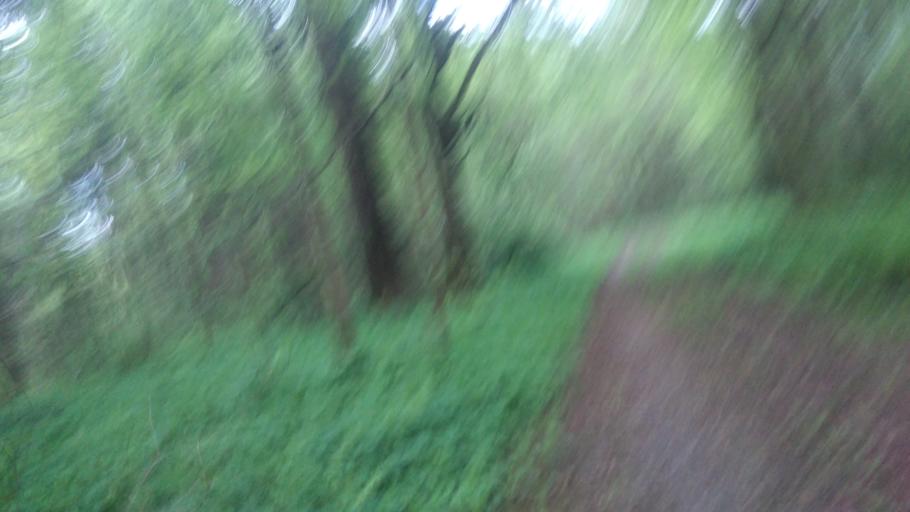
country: RU
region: Perm
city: Froly
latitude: 57.9665
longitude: 56.2968
